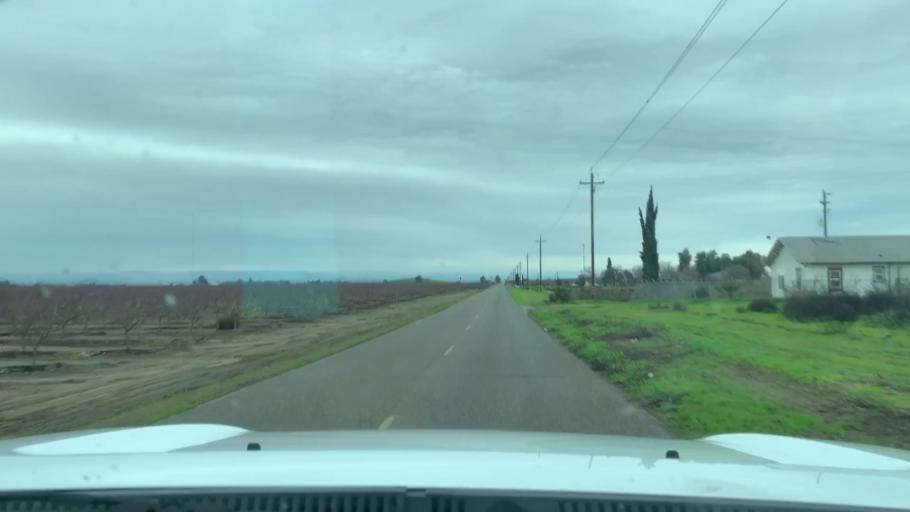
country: US
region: California
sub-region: Fresno County
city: Caruthers
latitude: 36.5474
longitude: -119.7718
